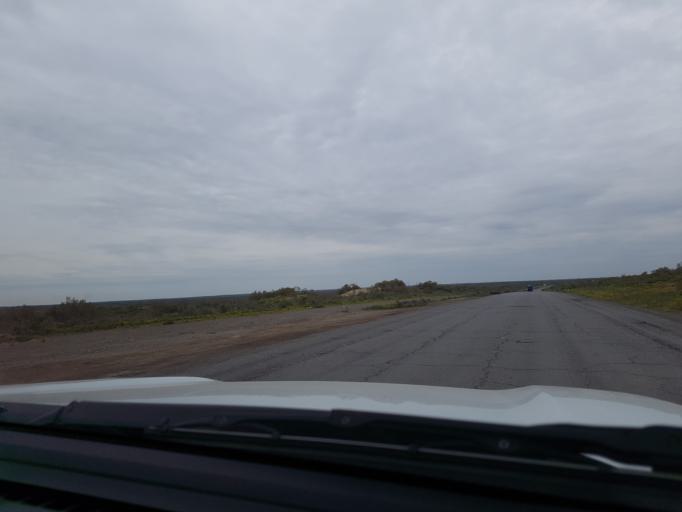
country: TM
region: Mary
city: Bayramaly
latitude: 37.8820
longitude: 62.6138
